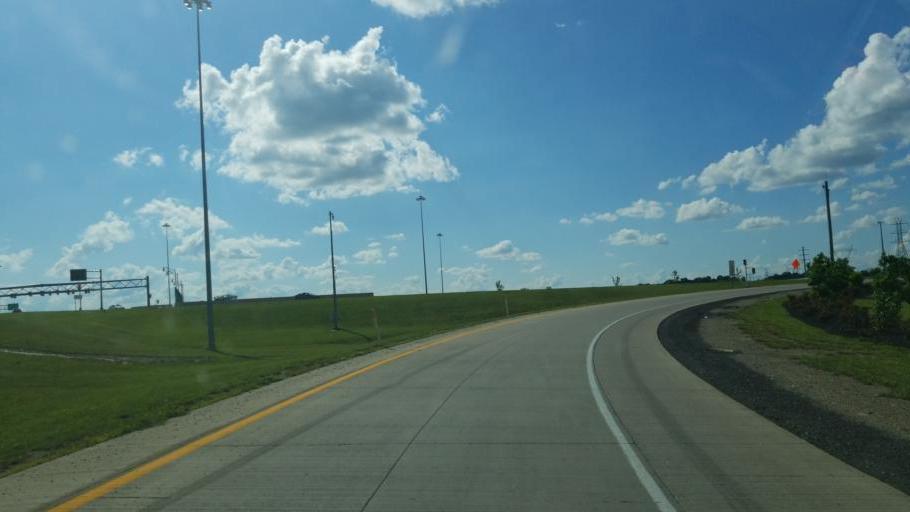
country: US
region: Ohio
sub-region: Franklin County
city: Grove City
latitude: 39.8405
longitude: -83.0880
